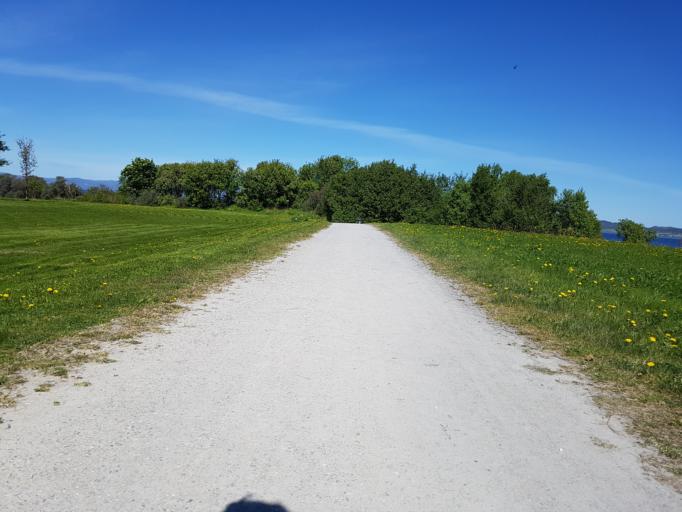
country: NO
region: Sor-Trondelag
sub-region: Malvik
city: Malvik
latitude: 63.4347
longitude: 10.7276
